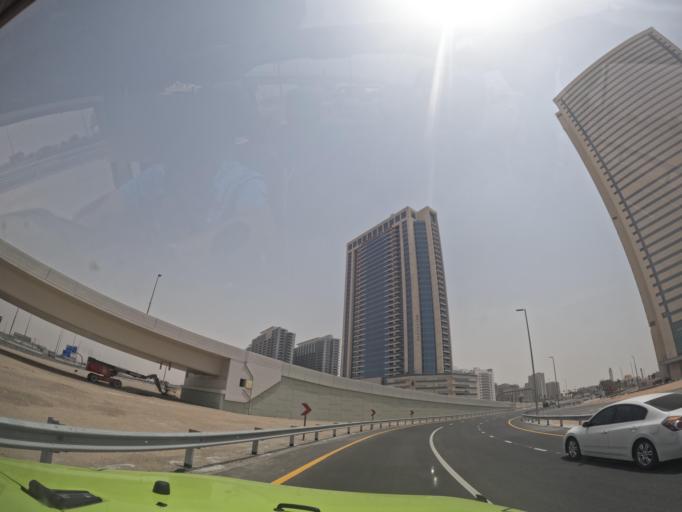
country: AE
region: Dubai
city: Dubai
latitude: 25.0955
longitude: 55.3843
